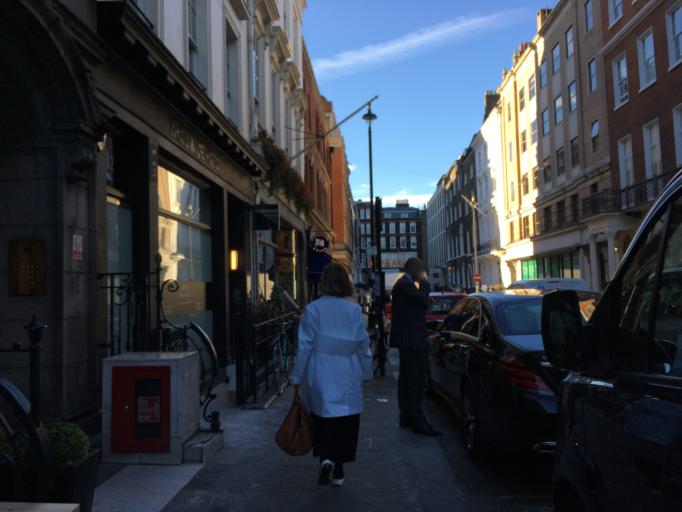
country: GB
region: England
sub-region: Greater London
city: London
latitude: 51.5090
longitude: -0.1427
